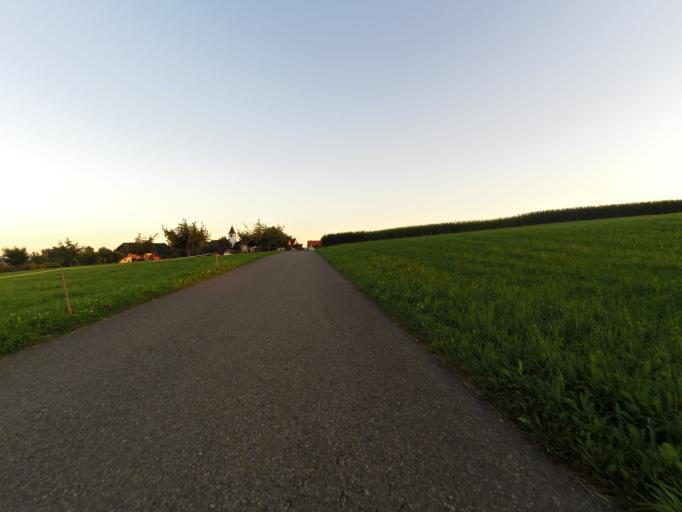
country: CH
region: Thurgau
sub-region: Weinfelden District
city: Wigoltingen
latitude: 47.5679
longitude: 9.0337
